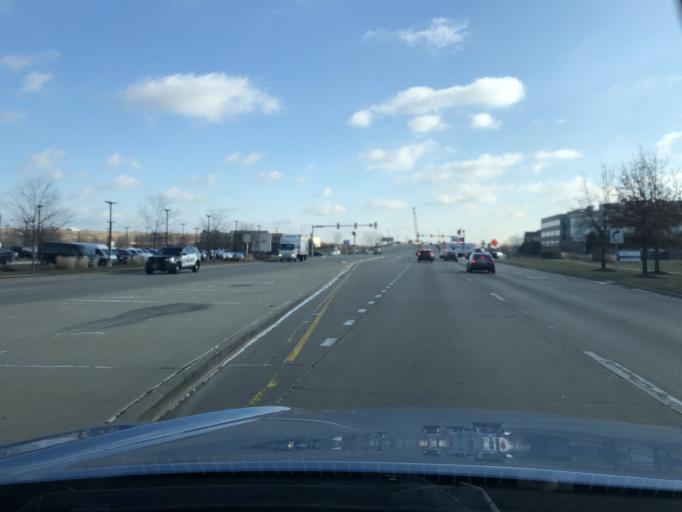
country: US
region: Illinois
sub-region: Cook County
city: Northbrook
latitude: 42.1055
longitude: -87.8253
